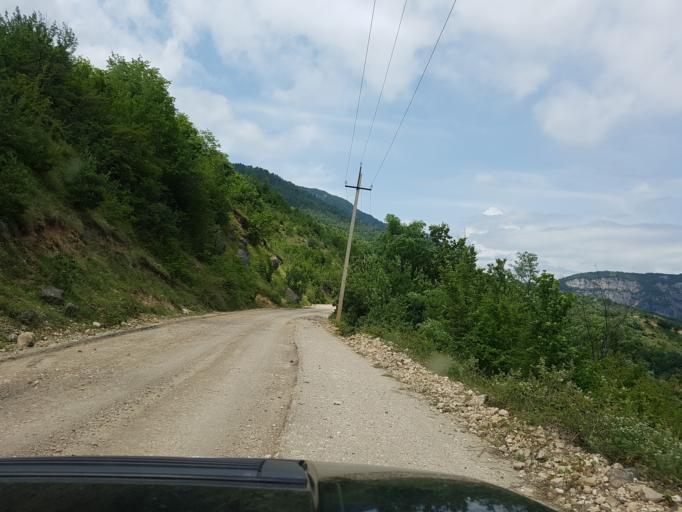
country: GE
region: Imereti
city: Tsqaltubo
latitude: 42.4943
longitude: 42.7842
